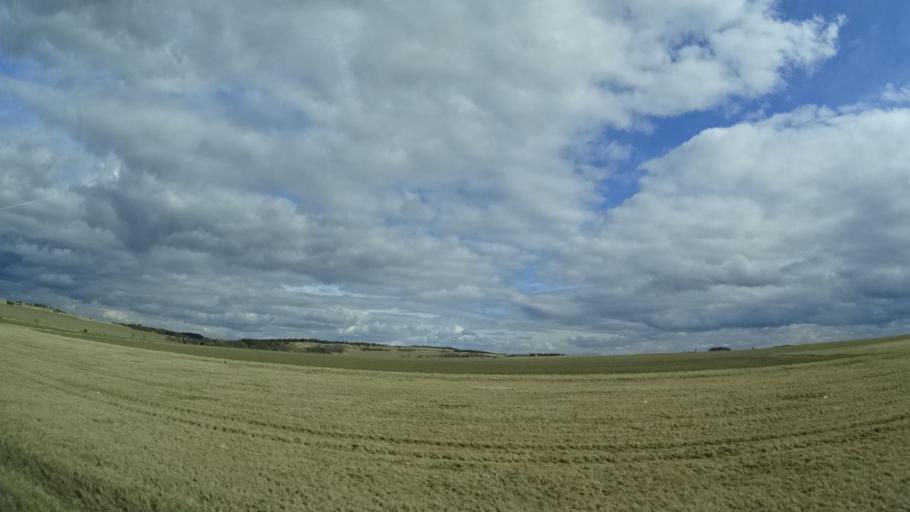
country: DE
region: Thuringia
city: Blankenhain
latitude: 50.8362
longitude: 11.3420
